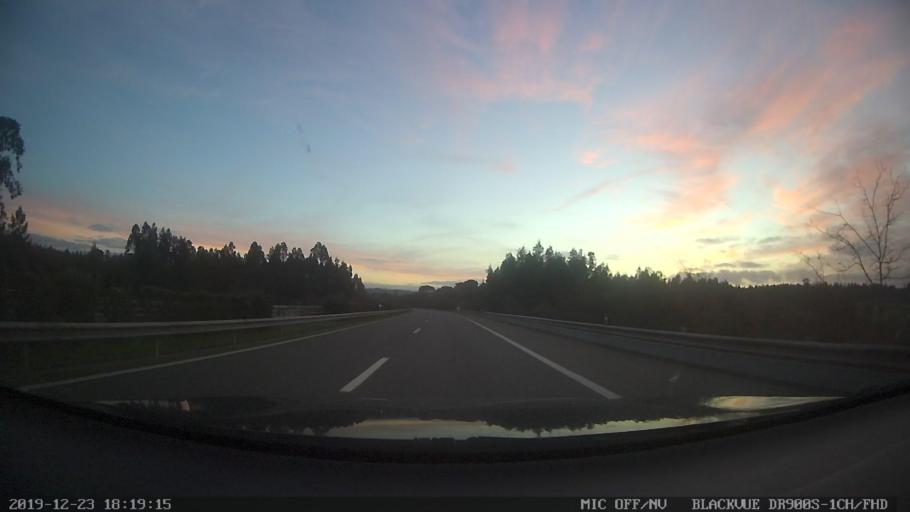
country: PT
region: Coimbra
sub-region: Condeixa-A-Nova
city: Condeixa-a-Nova
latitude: 40.1142
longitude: -8.5242
